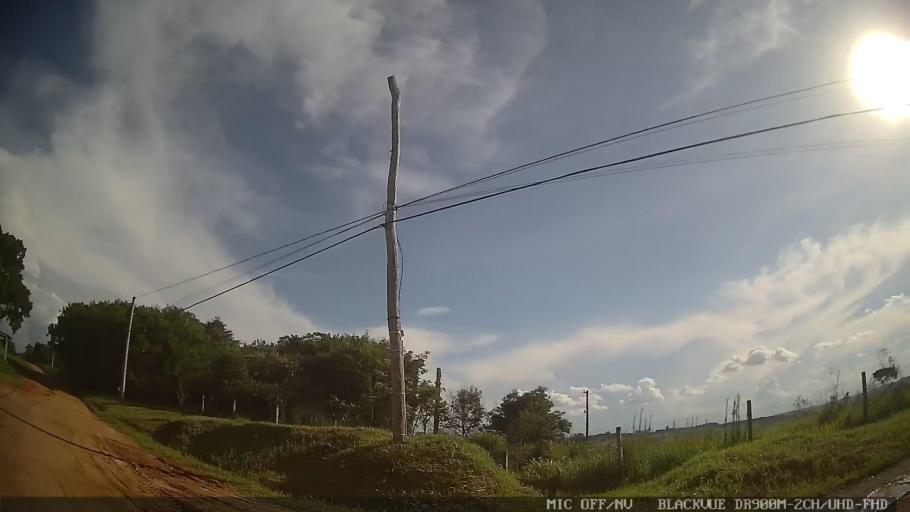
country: BR
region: Sao Paulo
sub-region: Tiete
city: Tiete
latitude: -23.0976
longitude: -47.7754
